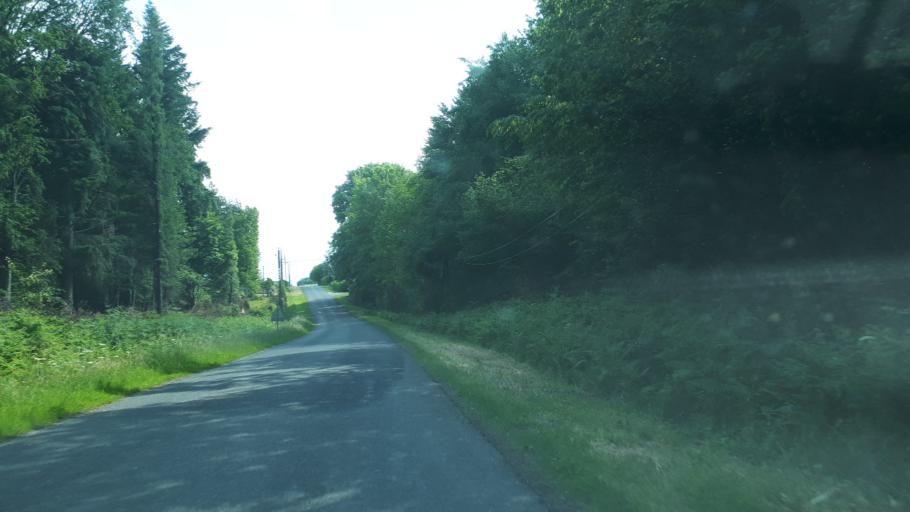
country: FR
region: Centre
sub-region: Departement du Cher
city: Henrichemont
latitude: 47.3736
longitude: 2.5942
